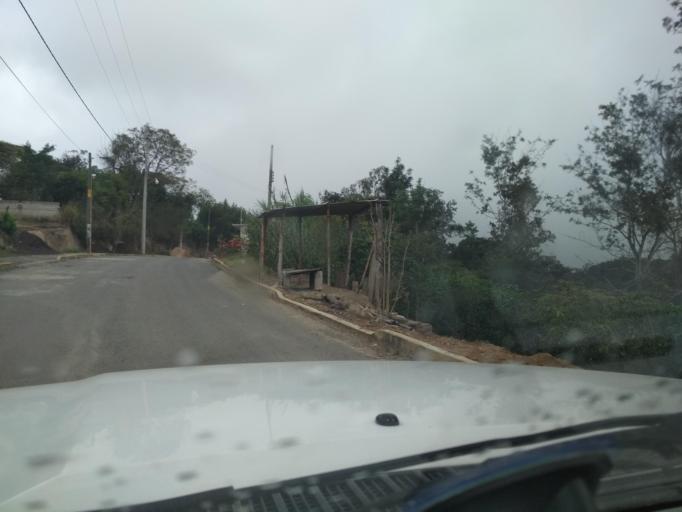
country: MX
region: Veracruz
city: El Castillo
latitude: 19.5403
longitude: -96.8245
